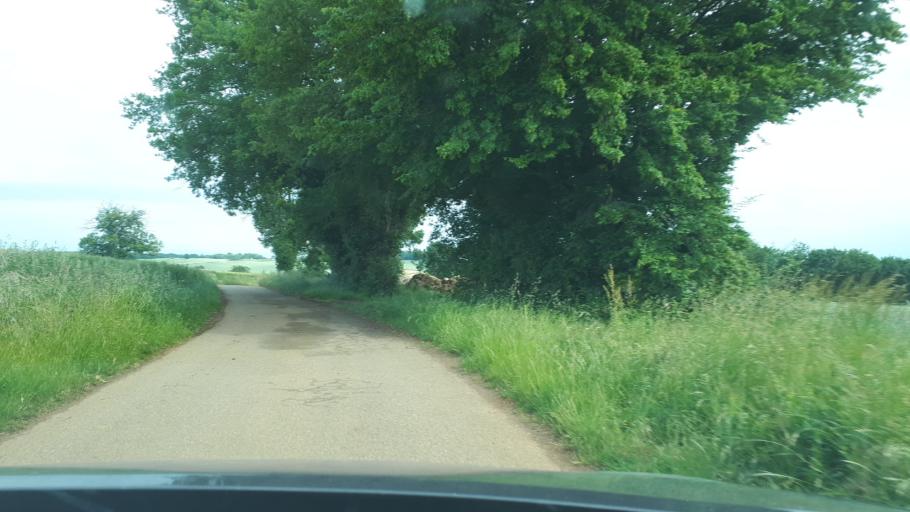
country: FR
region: Centre
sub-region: Departement du Cher
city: Sancerre
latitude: 47.3244
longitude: 2.7230
